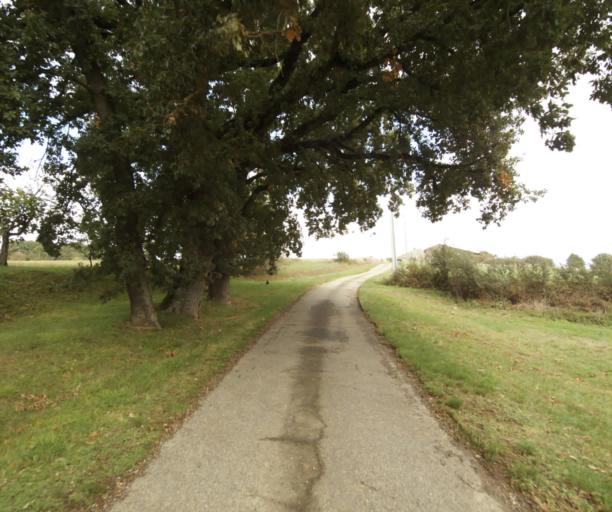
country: FR
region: Midi-Pyrenees
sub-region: Departement du Tarn-et-Garonne
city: Beaumont-de-Lomagne
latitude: 43.8714
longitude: 1.1045
